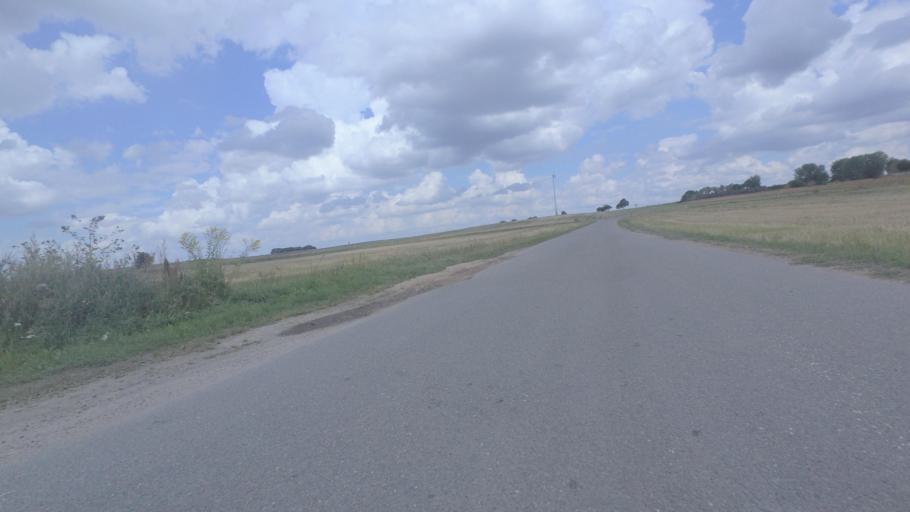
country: DE
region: Brandenburg
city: Wittstock
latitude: 53.1934
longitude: 12.4634
